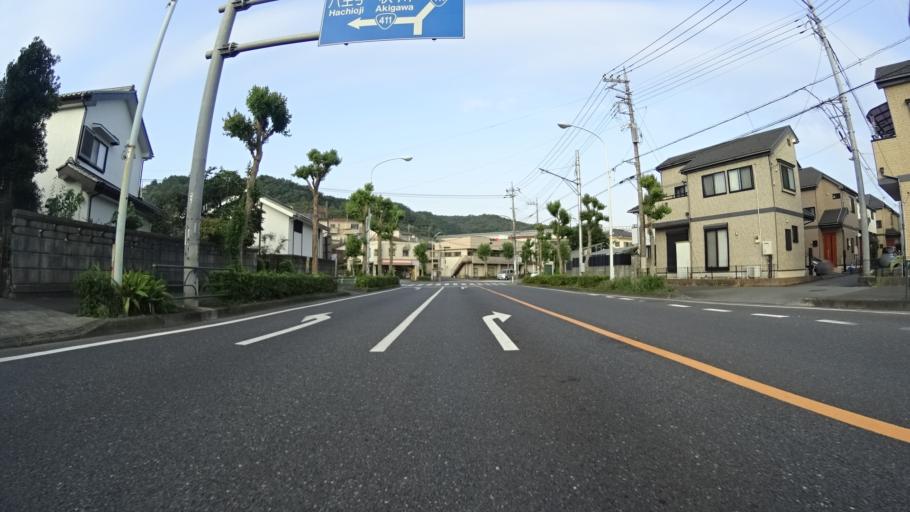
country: JP
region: Tokyo
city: Fussa
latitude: 35.7715
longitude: 139.2927
